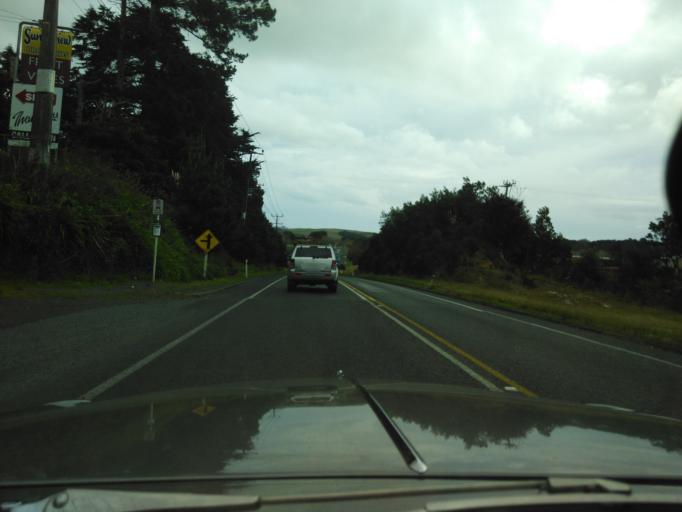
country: NZ
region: Auckland
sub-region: Auckland
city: Muriwai Beach
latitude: -36.7667
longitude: 174.5163
